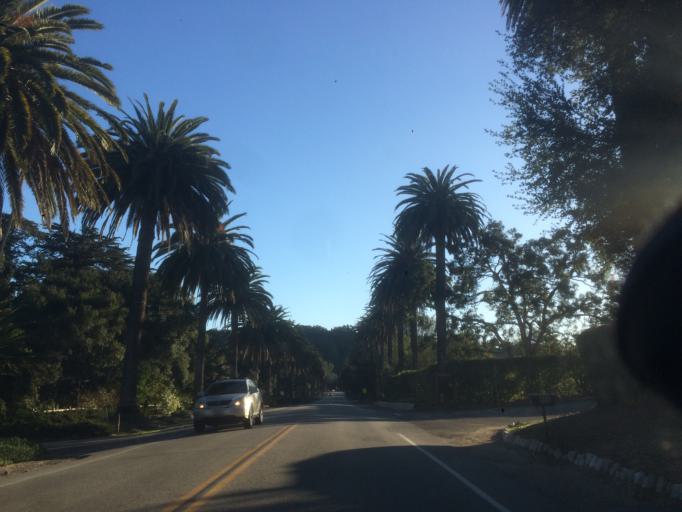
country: US
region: California
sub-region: Santa Barbara County
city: Mission Canyon
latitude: 34.4281
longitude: -119.7633
